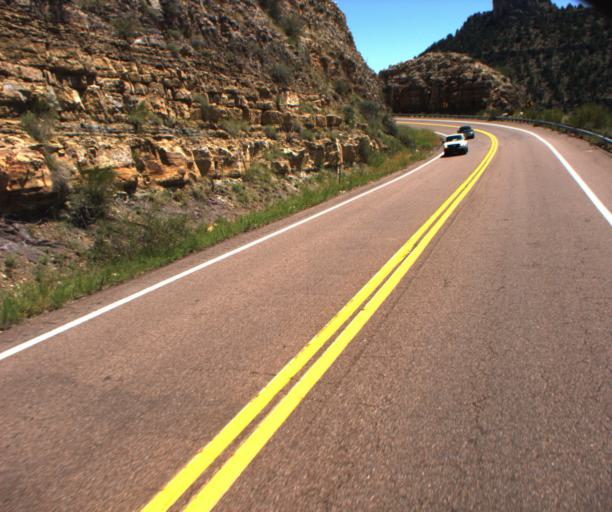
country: US
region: Arizona
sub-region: Navajo County
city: Cibecue
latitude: 33.8085
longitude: -110.4674
